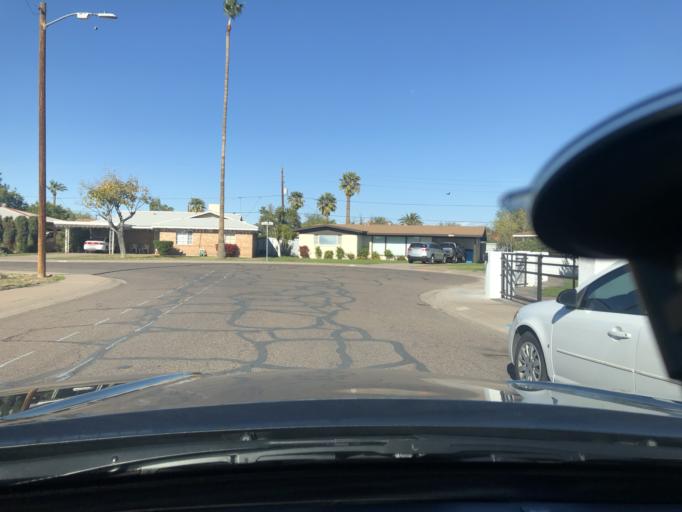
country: US
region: Arizona
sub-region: Maricopa County
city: Phoenix
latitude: 33.4682
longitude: -112.0401
